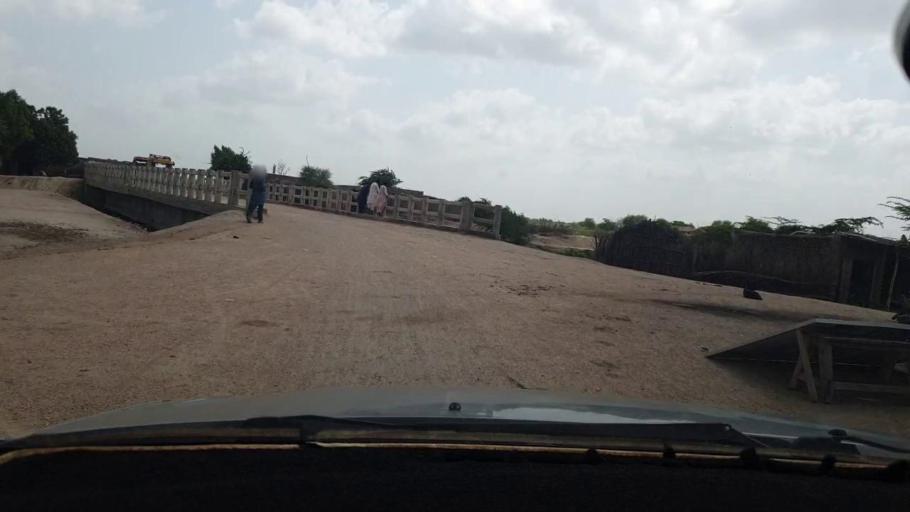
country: PK
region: Sindh
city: Tando Bago
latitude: 24.7205
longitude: 69.1713
